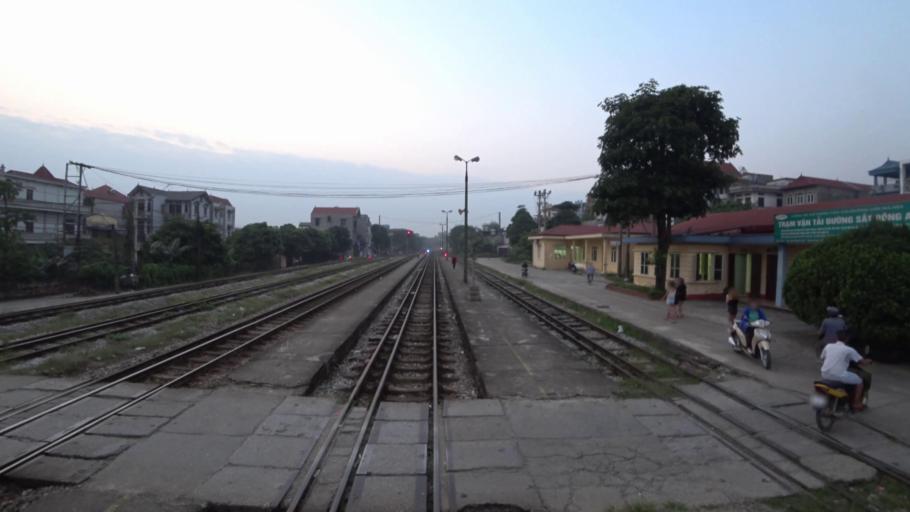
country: VN
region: Ha Noi
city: Soc Son
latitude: 21.2299
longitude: 105.8611
